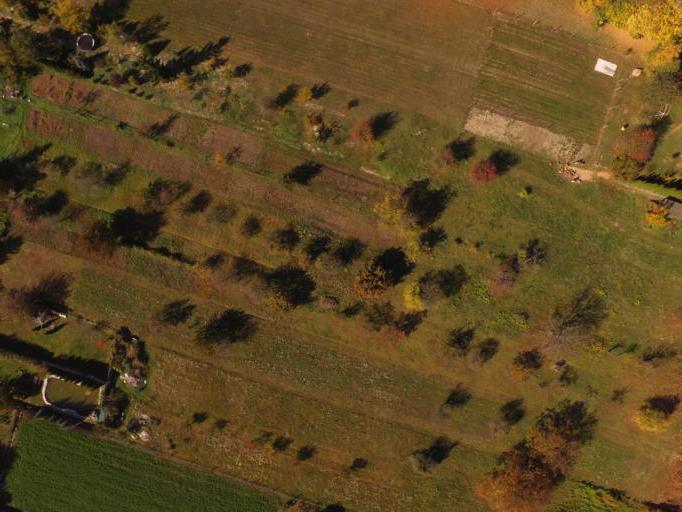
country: HU
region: Fejer
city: Many
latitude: 47.5202
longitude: 18.6170
